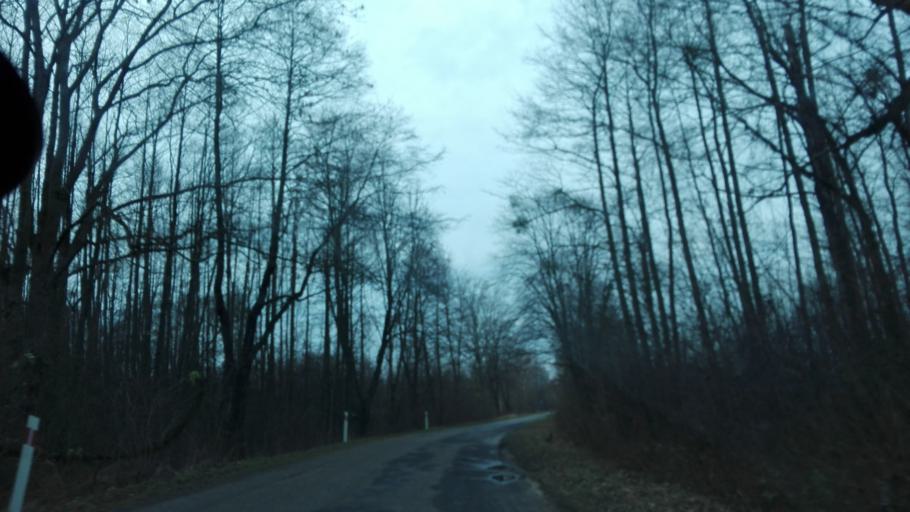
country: PL
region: Lublin Voivodeship
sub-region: Powiat bialski
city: Sosnowka
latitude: 51.7307
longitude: 23.4172
